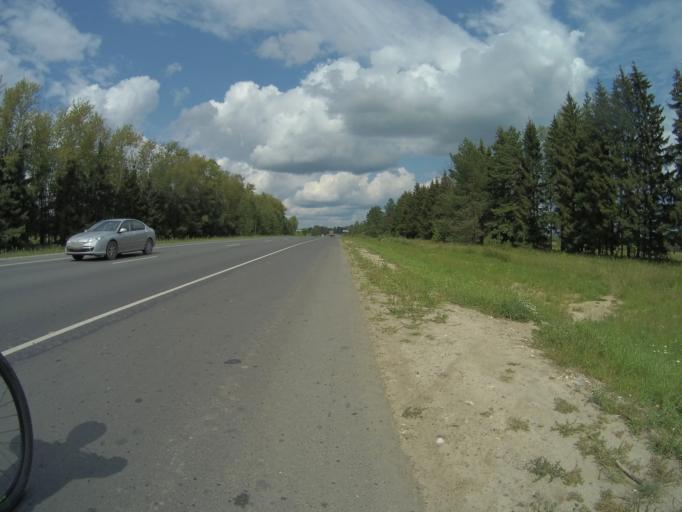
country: RU
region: Vladimir
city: Kideksha
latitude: 56.5631
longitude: 40.5502
